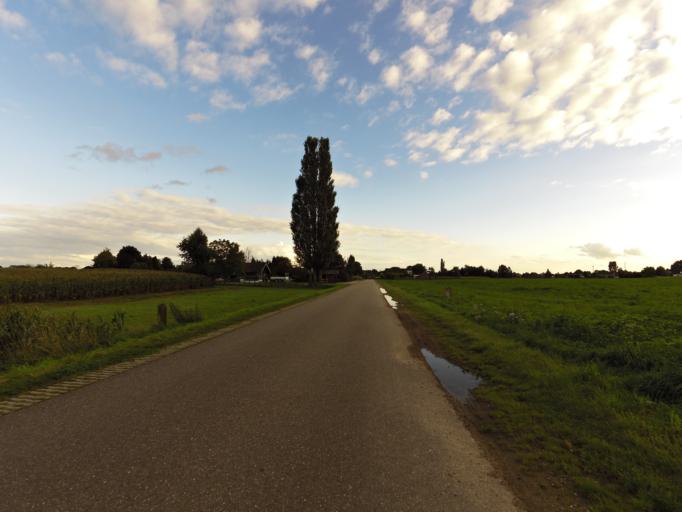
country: NL
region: Gelderland
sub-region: Gemeente Montferland
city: s-Heerenberg
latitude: 51.8895
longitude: 6.2644
